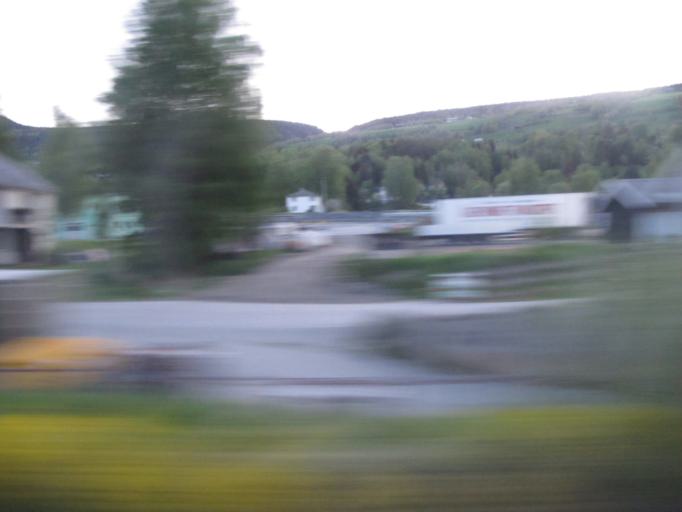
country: NO
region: Oppland
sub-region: Sor-Fron
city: Hundorp
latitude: 61.5655
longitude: 9.9152
